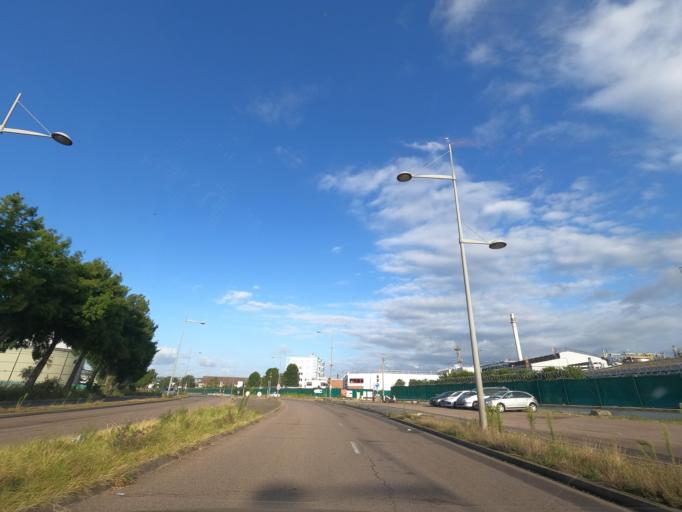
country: FR
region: Haute-Normandie
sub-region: Departement de la Seine-Maritime
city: Le Petit-Quevilly
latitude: 49.4374
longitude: 1.0568
